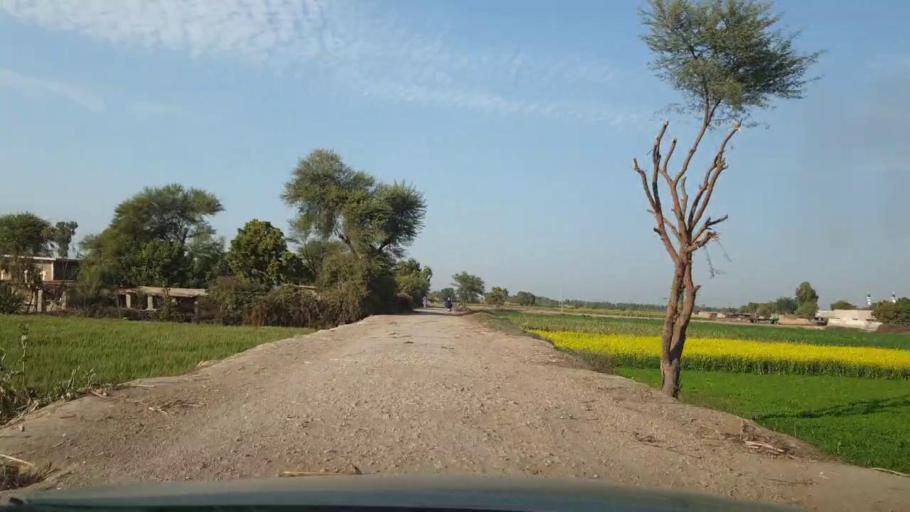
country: PK
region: Sindh
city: Tando Allahyar
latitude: 25.6008
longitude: 68.6722
